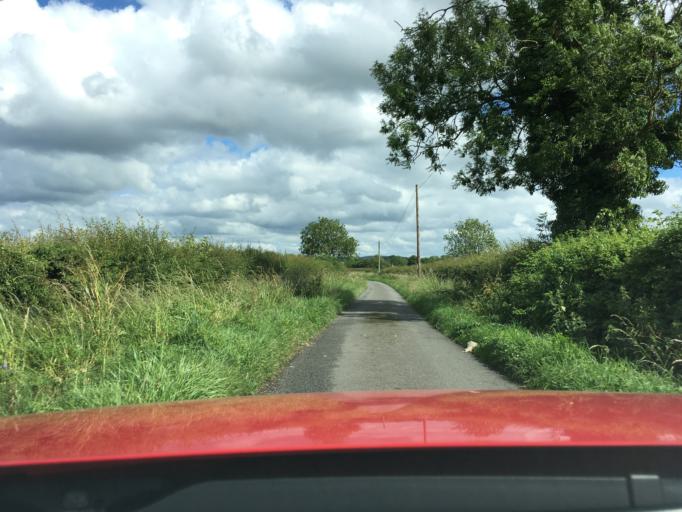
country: GB
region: England
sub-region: Gloucestershire
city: Stonehouse
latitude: 51.8249
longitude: -2.3548
